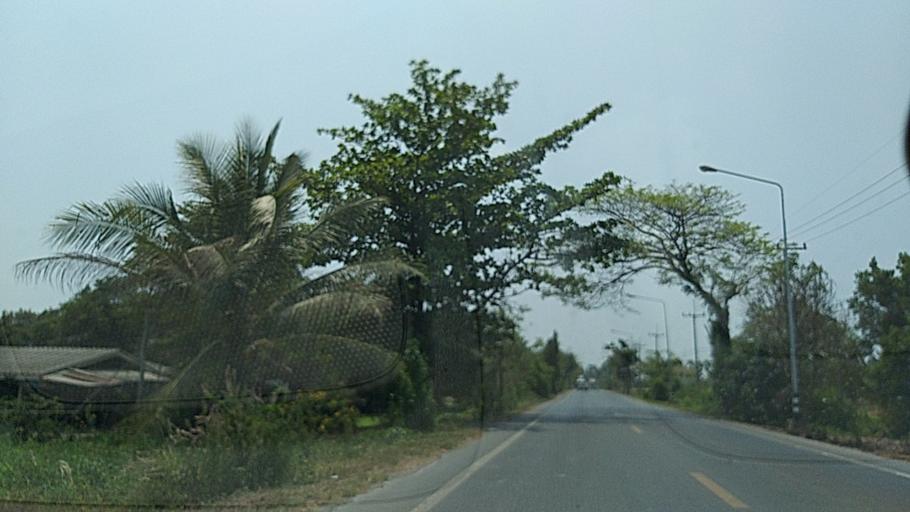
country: TH
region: Chachoengsao
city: Bang Nam Priao
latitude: 13.8833
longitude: 100.9691
